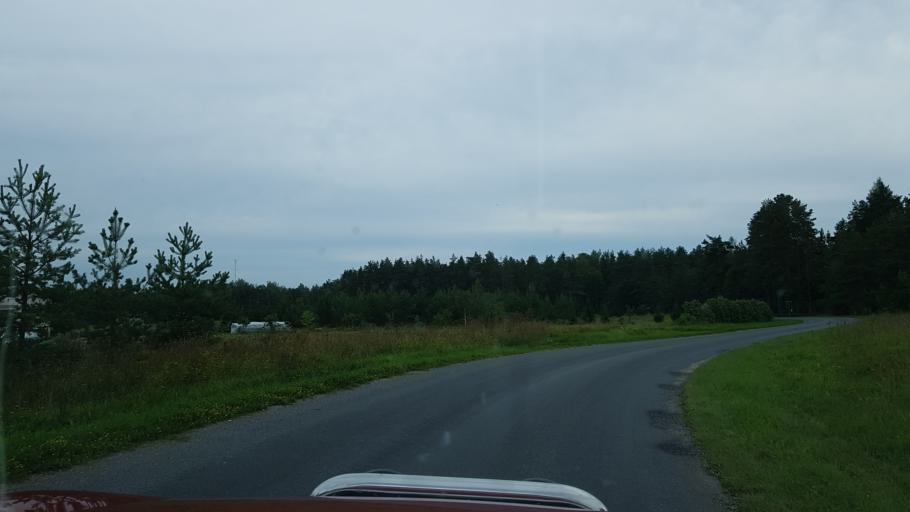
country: EE
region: Laeaene
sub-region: Ridala Parish
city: Uuemoisa
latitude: 59.0106
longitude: 23.7247
